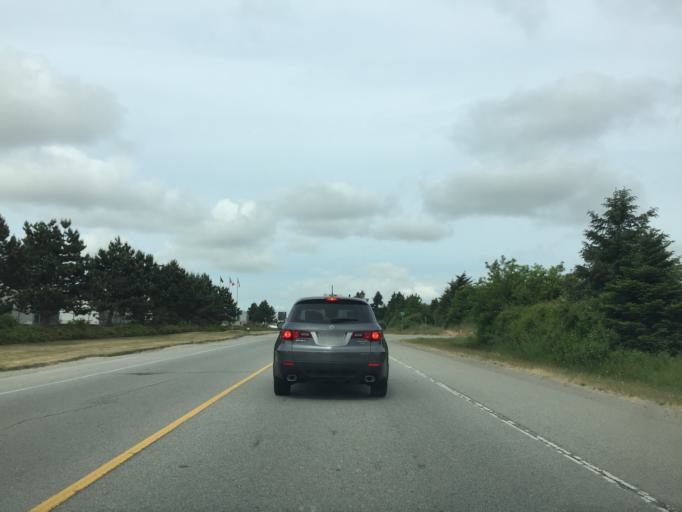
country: CA
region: British Columbia
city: Richmond
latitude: 49.2053
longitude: -123.1598
